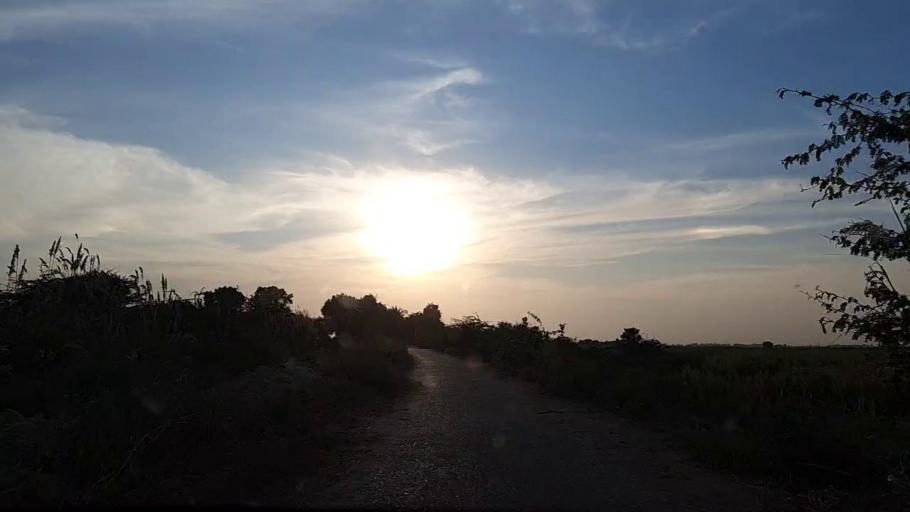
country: PK
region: Sindh
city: Mirpur Batoro
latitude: 24.6424
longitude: 68.1426
